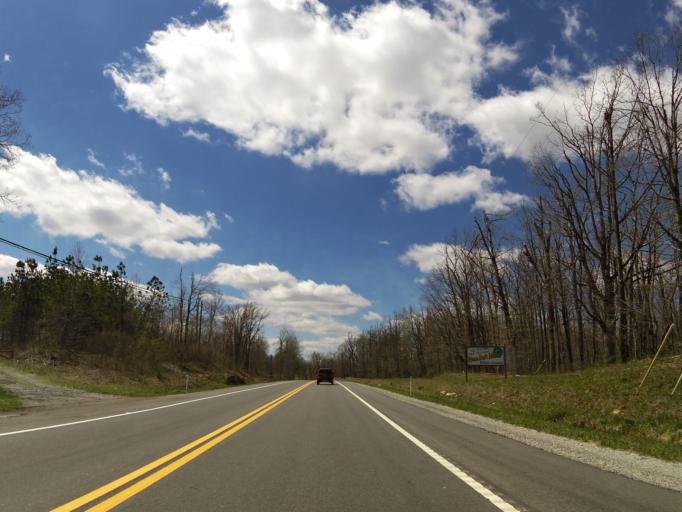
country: US
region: Tennessee
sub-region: Putnam County
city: Monterey
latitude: 35.9622
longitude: -85.2807
